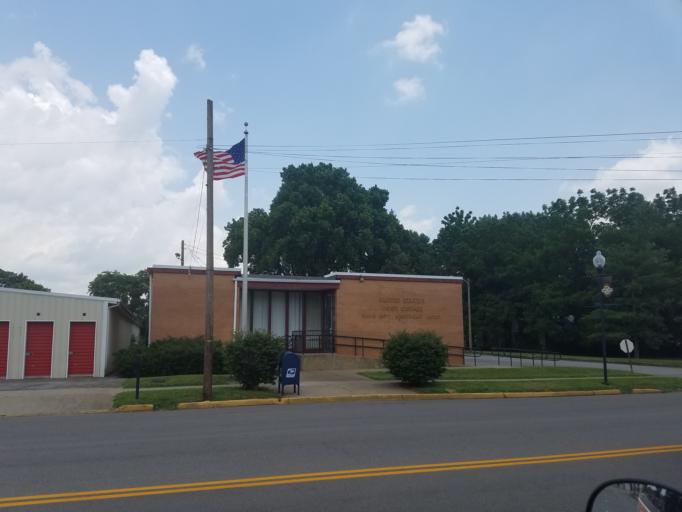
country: US
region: Kentucky
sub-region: Barren County
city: Cave City
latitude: 37.1365
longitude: -85.9571
